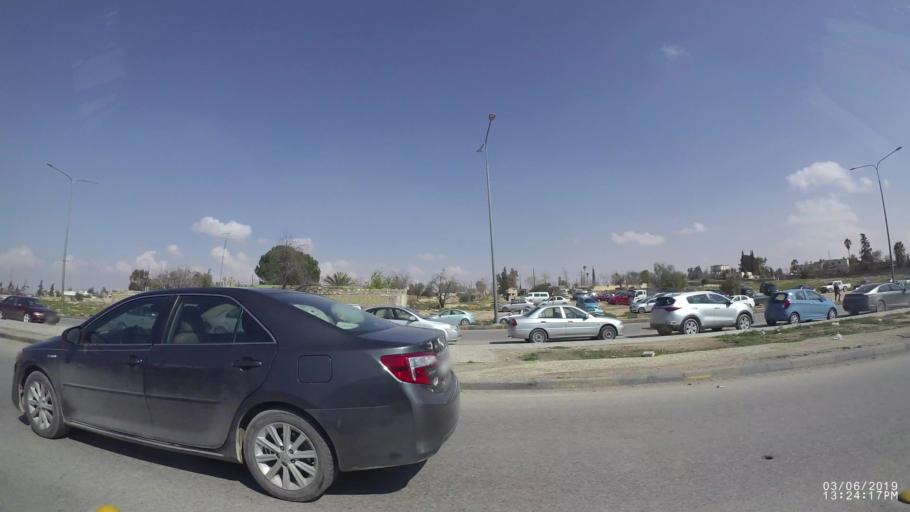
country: JO
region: Zarqa
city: Zarqa
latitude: 32.0591
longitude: 36.0944
